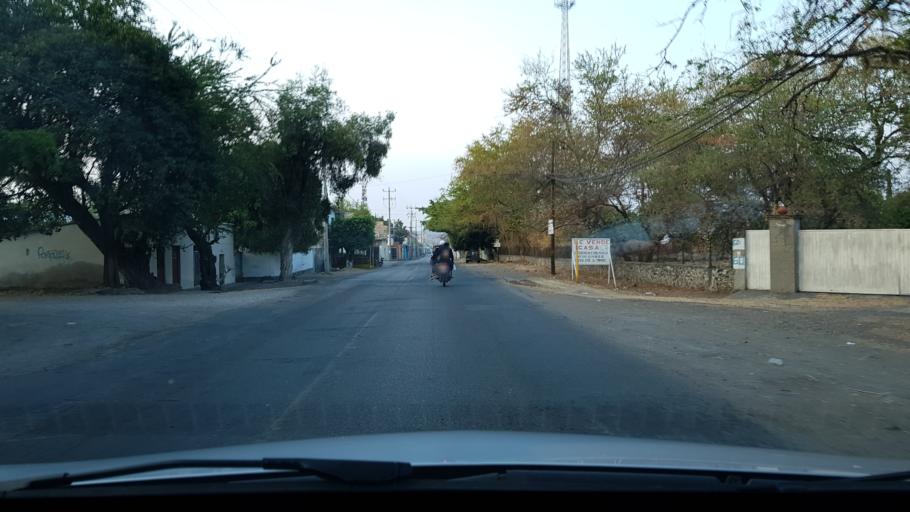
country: MX
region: Morelos
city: Jonacatepec de Leandro Valle
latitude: 18.6878
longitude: -98.8024
